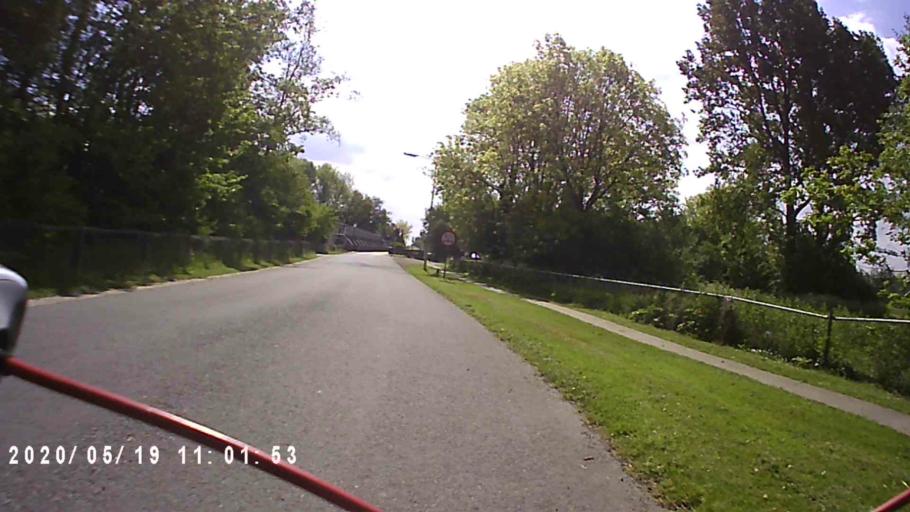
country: NL
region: Groningen
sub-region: Gemeente Zuidhorn
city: Grijpskerk
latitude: 53.3015
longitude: 6.2750
